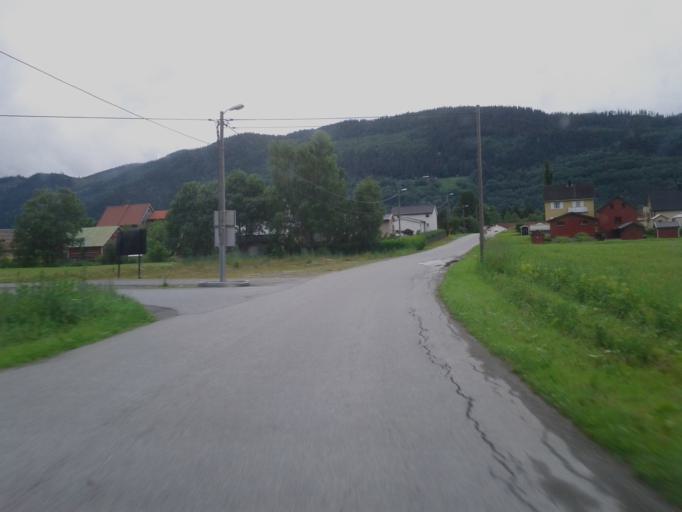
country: NO
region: Sor-Trondelag
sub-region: Melhus
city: Lundamo
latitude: 63.1516
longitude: 10.2935
